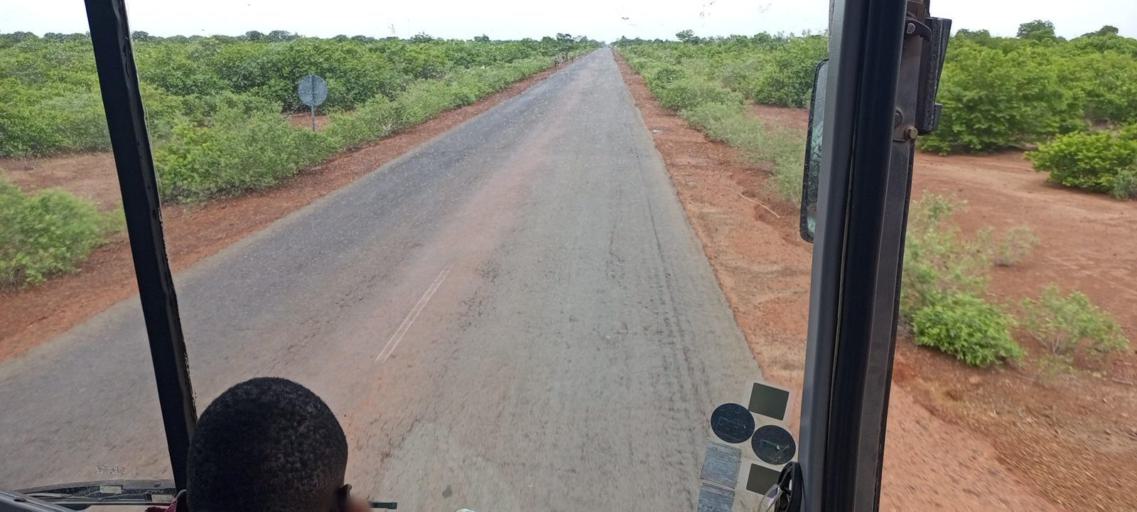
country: ML
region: Sikasso
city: Koutiala
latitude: 12.5513
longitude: -5.5849
